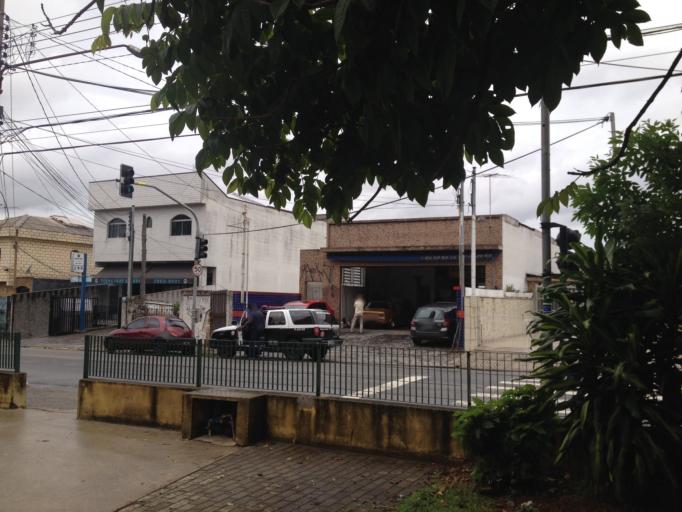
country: BR
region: Sao Paulo
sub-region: Sao Caetano Do Sul
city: Sao Caetano do Sul
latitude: -23.5680
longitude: -46.5697
